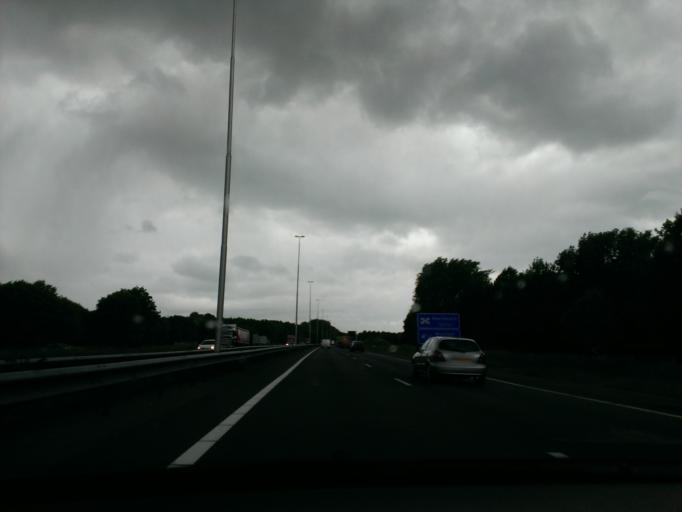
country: NL
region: Gelderland
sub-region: Gemeente Nijmegen
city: Lindenholt
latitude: 51.8075
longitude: 5.7850
